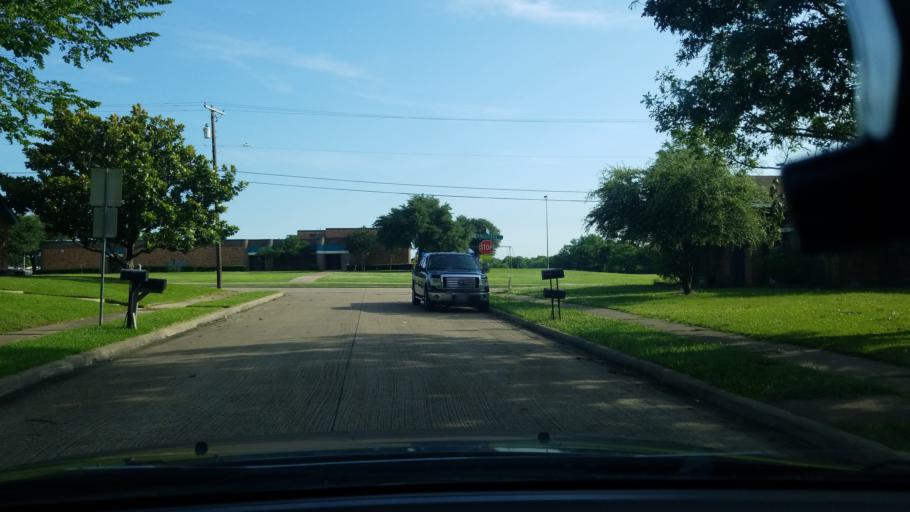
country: US
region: Texas
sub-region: Dallas County
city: Mesquite
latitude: 32.8045
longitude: -96.6048
